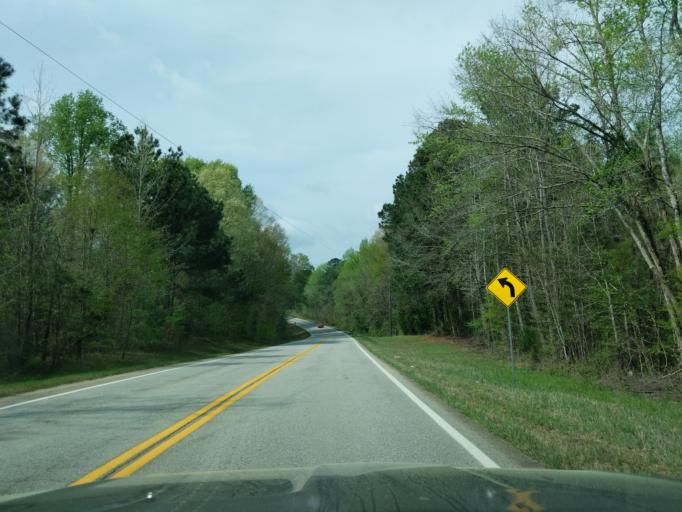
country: US
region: Georgia
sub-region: Lincoln County
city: Lincolnton
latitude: 33.7577
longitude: -82.3811
